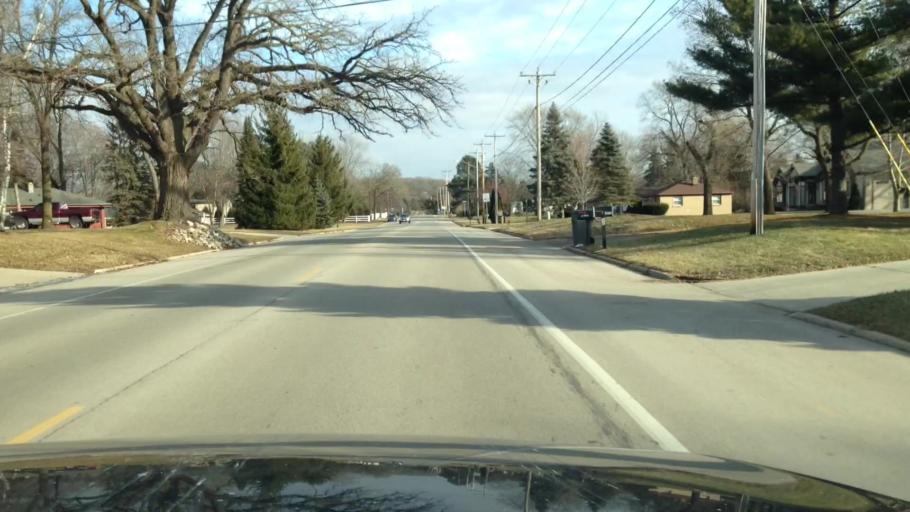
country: US
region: Wisconsin
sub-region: Waukesha County
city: Muskego
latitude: 42.9300
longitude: -88.1427
